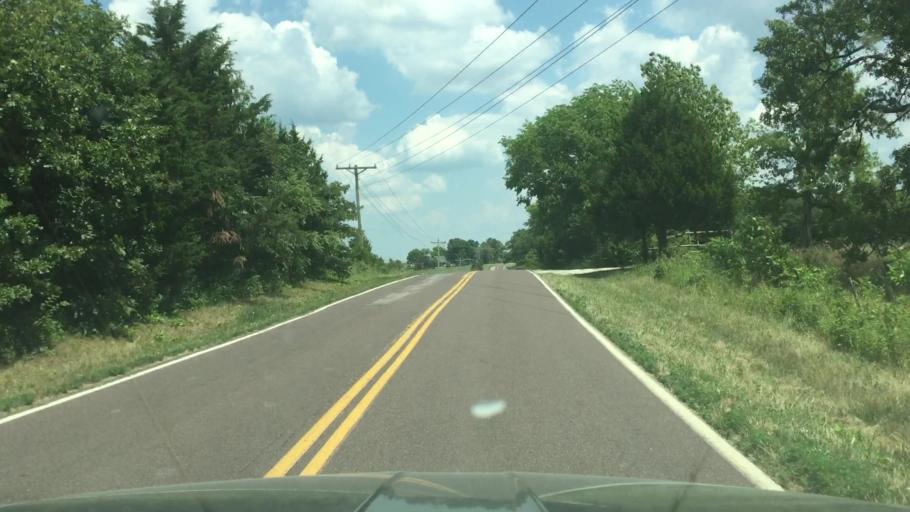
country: US
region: Missouri
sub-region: Miller County
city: Tuscumbia
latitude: 38.1208
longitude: -92.4694
